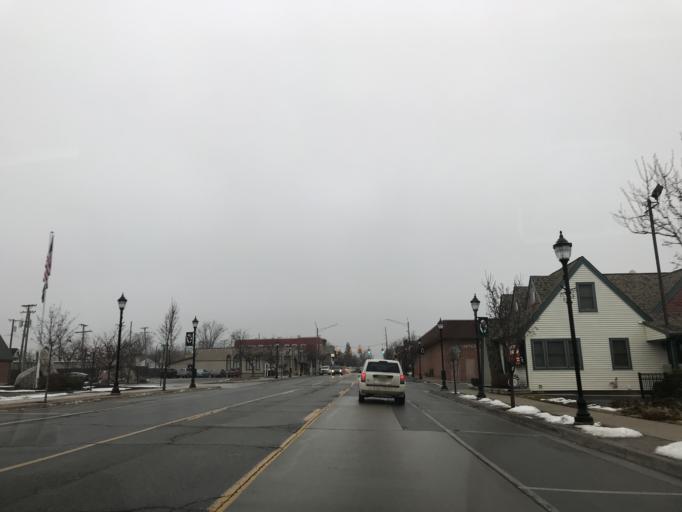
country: US
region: Michigan
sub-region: Oakland County
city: South Lyon
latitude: 42.4592
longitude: -83.6514
